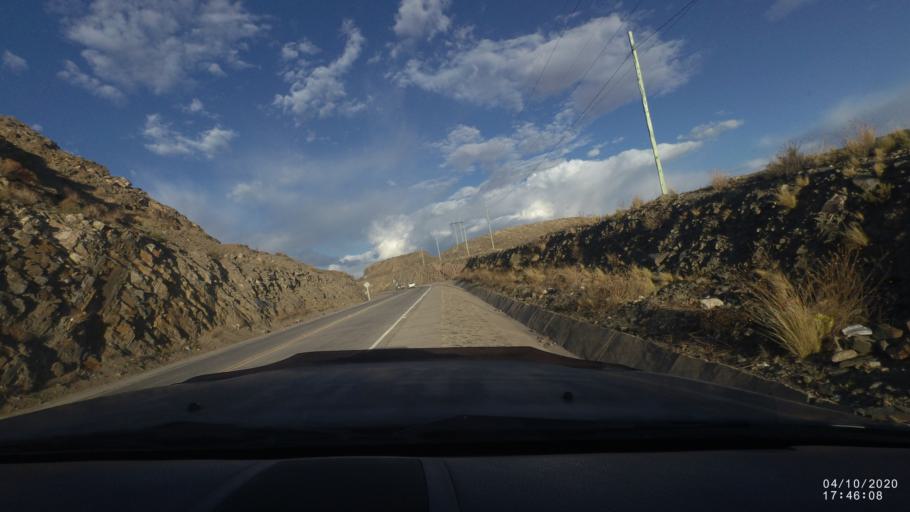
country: BO
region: Oruro
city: Oruro
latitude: -18.0318
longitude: -67.1495
